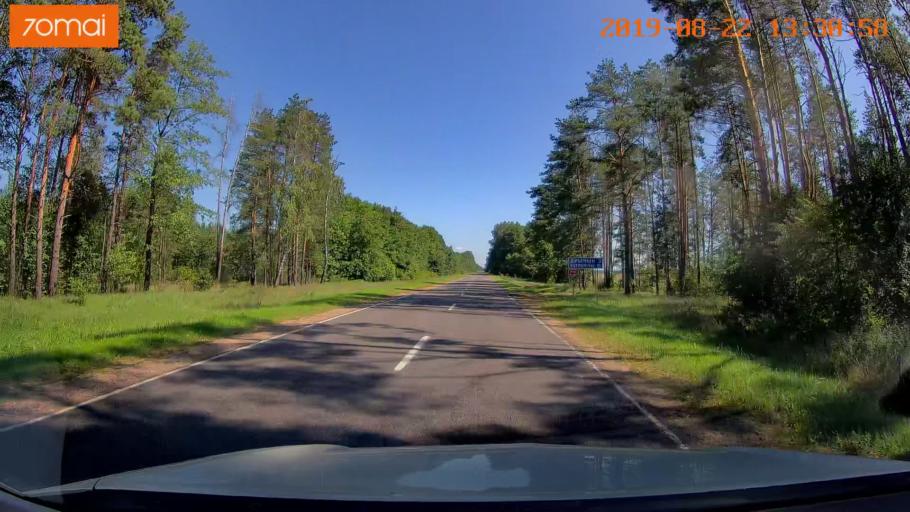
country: BY
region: Minsk
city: Staryya Darohi
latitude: 53.2173
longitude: 28.1679
